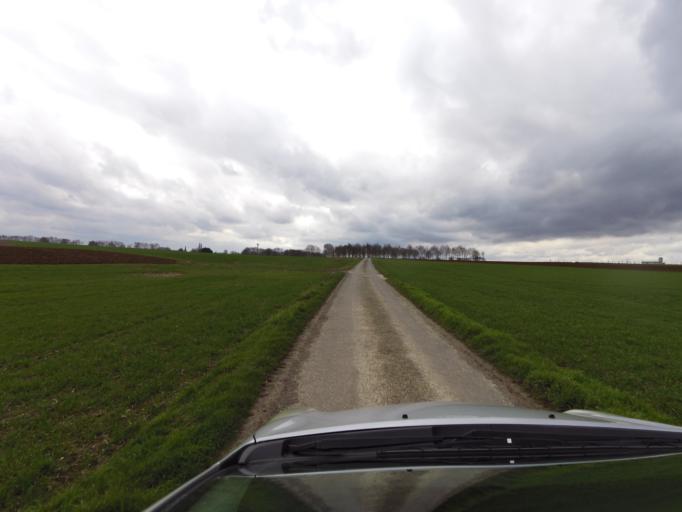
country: FR
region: Nord-Pas-de-Calais
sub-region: Departement du Pas-de-Calais
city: Agny
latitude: 50.2199
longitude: 2.7834
